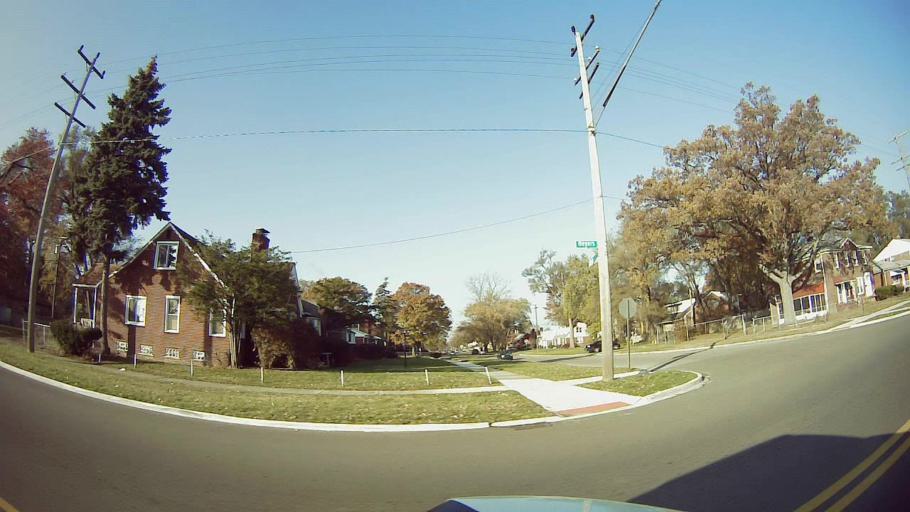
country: US
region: Michigan
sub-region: Oakland County
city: Oak Park
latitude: 42.4202
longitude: -83.1702
